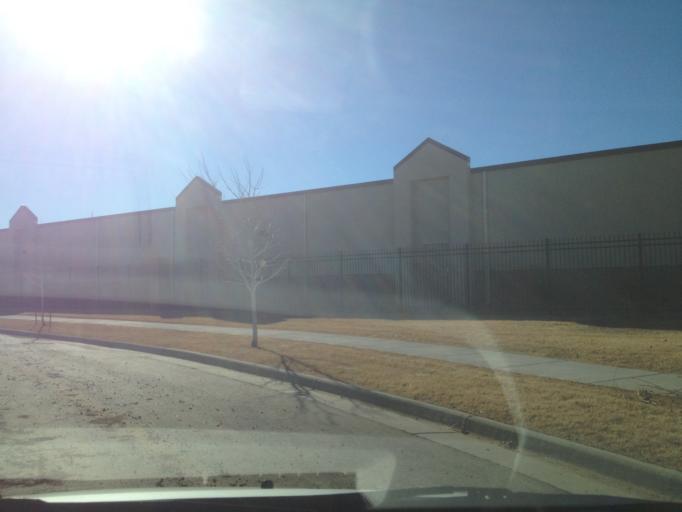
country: US
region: Colorado
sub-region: Weld County
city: Dacono
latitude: 40.0750
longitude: -104.9731
